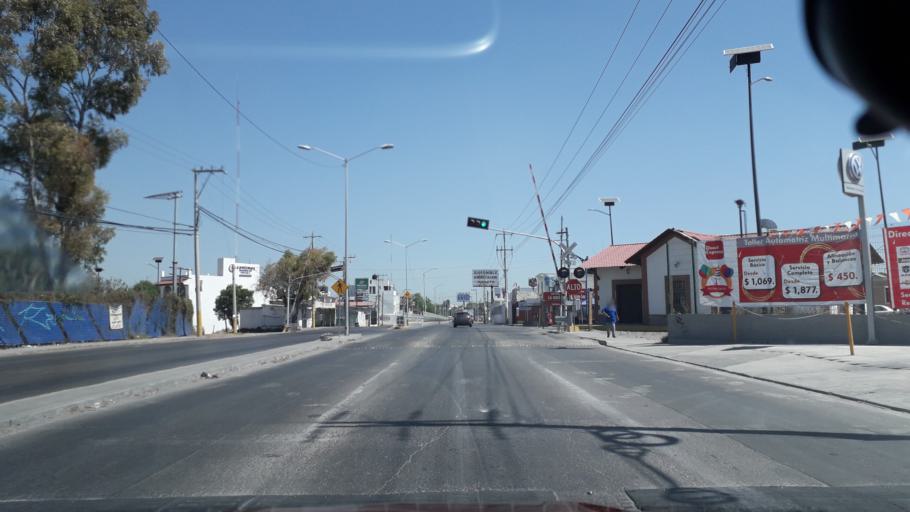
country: MX
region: Puebla
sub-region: Cuautlancingo
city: Sanctorum
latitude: 19.0813
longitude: -98.2388
